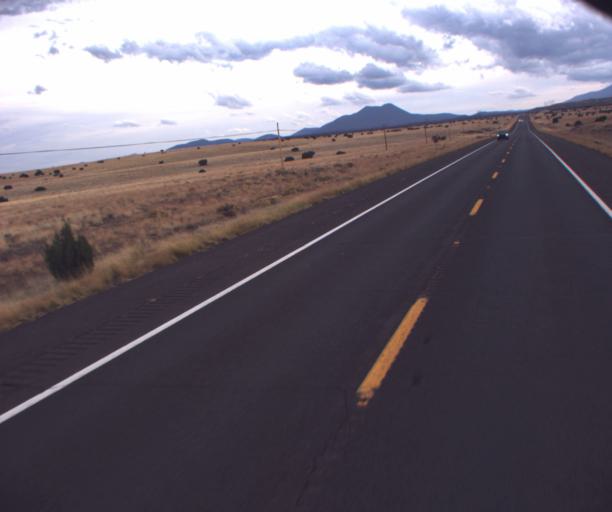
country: US
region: Arizona
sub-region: Coconino County
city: Flagstaff
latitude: 35.5562
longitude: -111.5354
